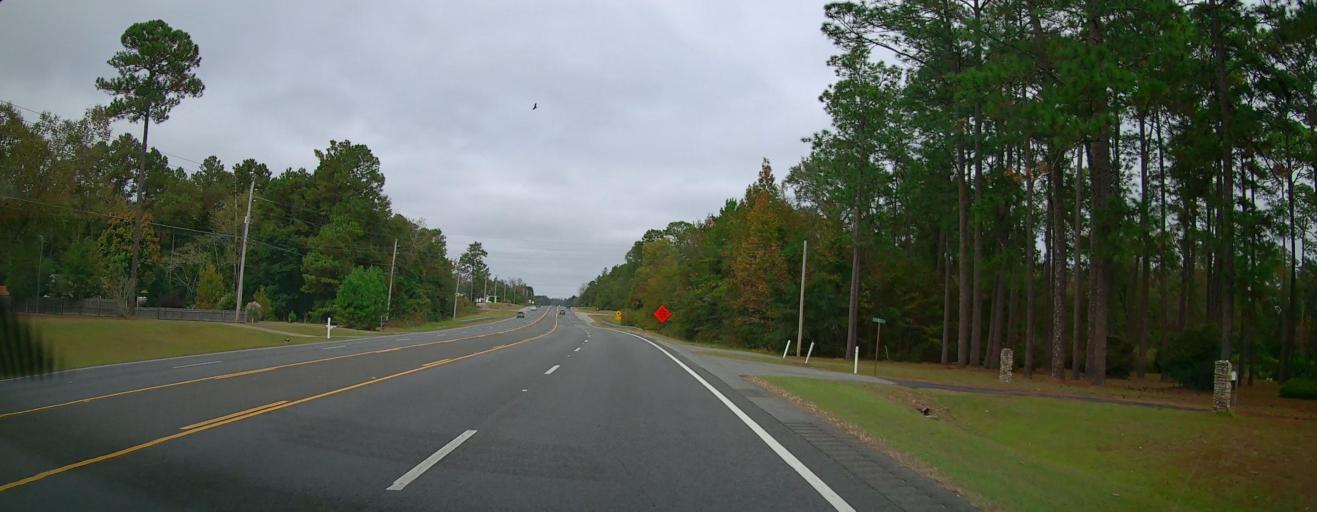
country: US
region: Georgia
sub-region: Thomas County
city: Thomasville
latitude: 30.9216
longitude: -83.9144
